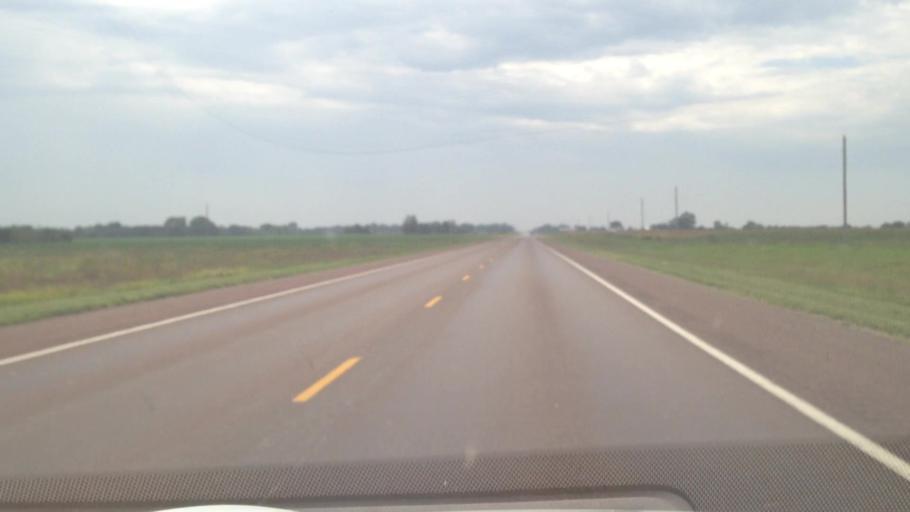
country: US
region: Kansas
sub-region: Crawford County
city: Girard
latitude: 37.4571
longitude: -94.8330
